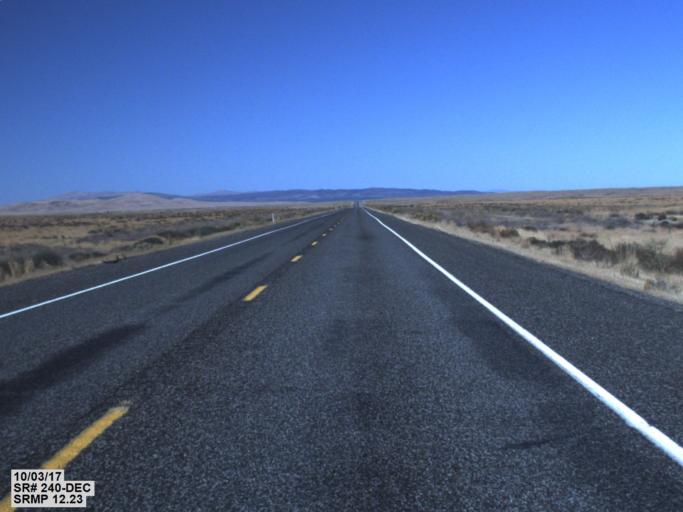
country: US
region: Washington
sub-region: Benton County
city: Benton City
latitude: 46.4675
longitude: -119.5423
